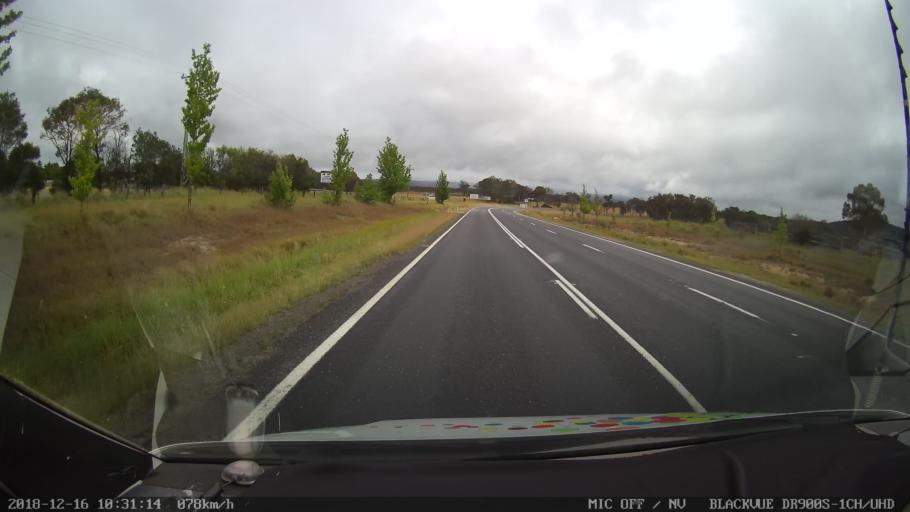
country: AU
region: New South Wales
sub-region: Tenterfield Municipality
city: Carrolls Creek
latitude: -29.0834
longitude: 152.0044
